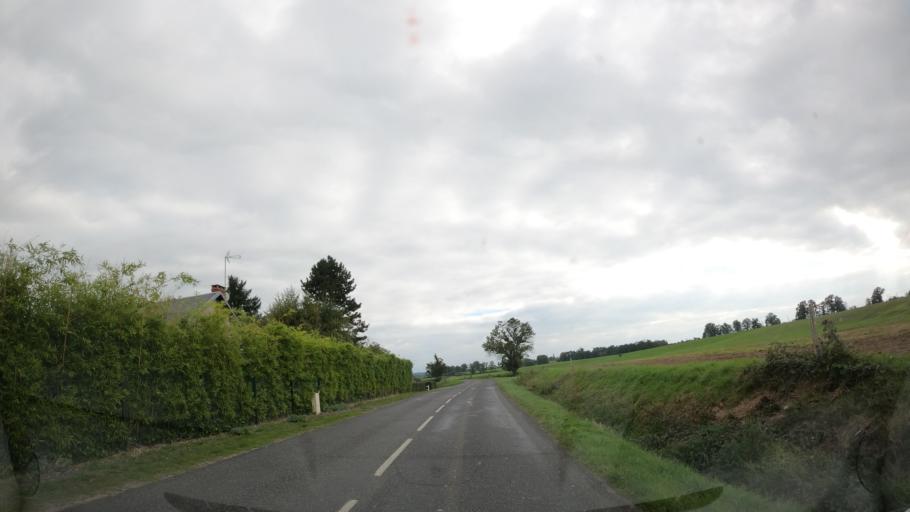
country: FR
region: Auvergne
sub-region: Departement de l'Allier
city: Lapalisse
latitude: 46.3203
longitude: 3.6337
